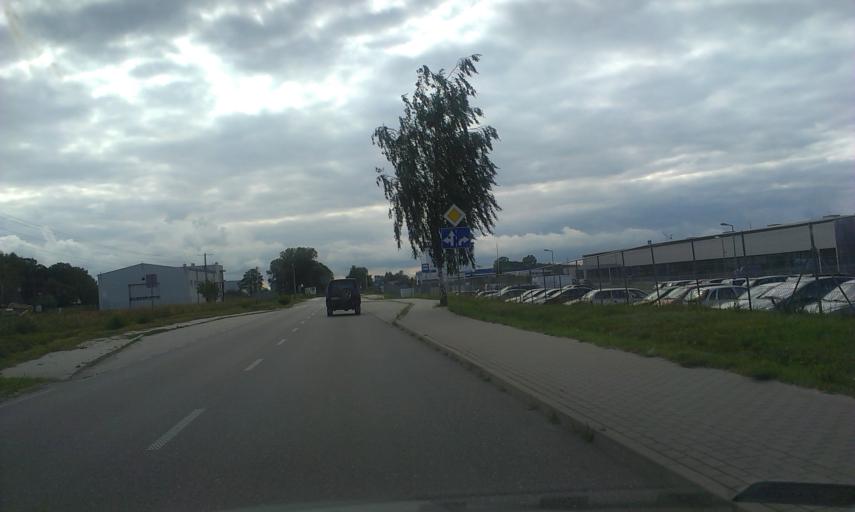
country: PL
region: Masovian Voivodeship
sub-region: Powiat zyrardowski
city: Radziejowice
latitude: 51.9728
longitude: 20.5580
